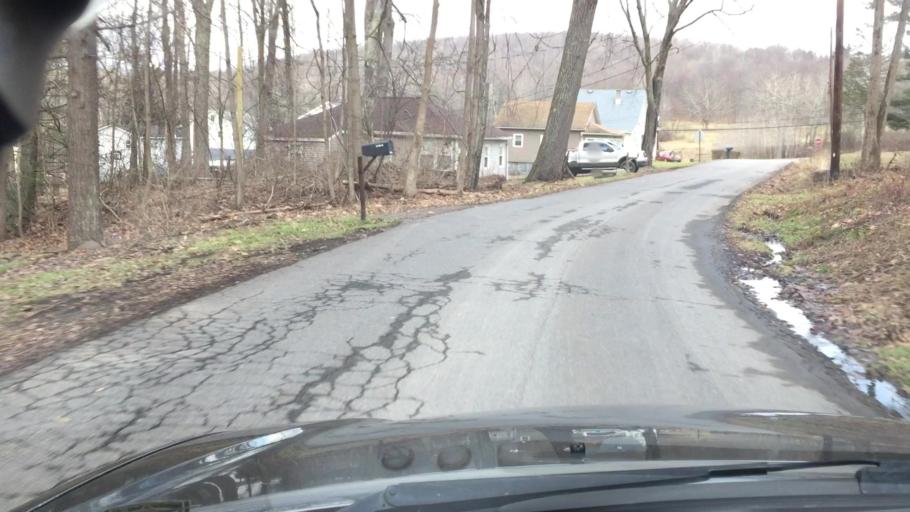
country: US
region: Pennsylvania
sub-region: Luzerne County
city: Harveys Lake
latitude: 41.3758
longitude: -76.0487
